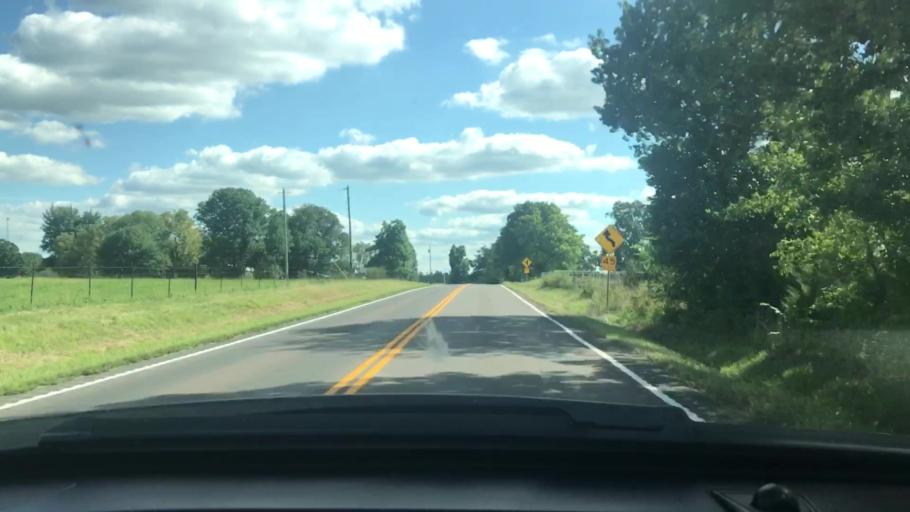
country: US
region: Missouri
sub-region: Wright County
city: Mountain Grove
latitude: 37.2586
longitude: -92.3082
